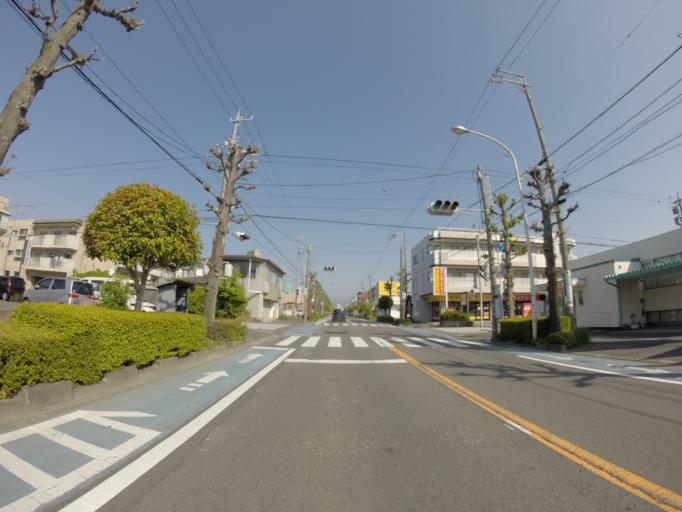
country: JP
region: Shizuoka
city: Shizuoka-shi
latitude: 34.9442
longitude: 138.3750
